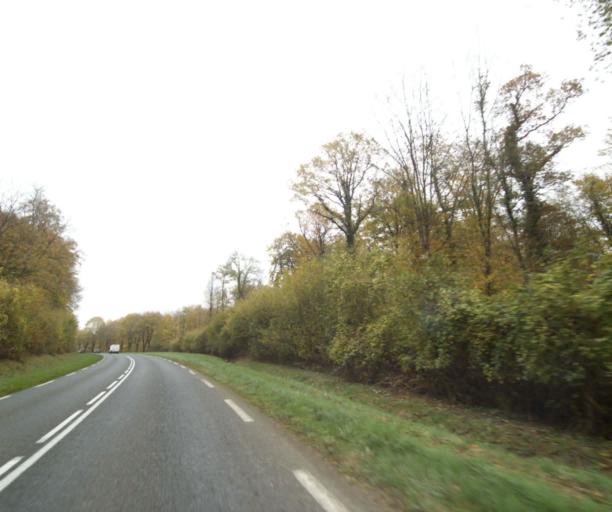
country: FR
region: Lorraine
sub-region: Departement de Meurthe-et-Moselle
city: Briey
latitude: 49.2723
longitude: 5.9573
